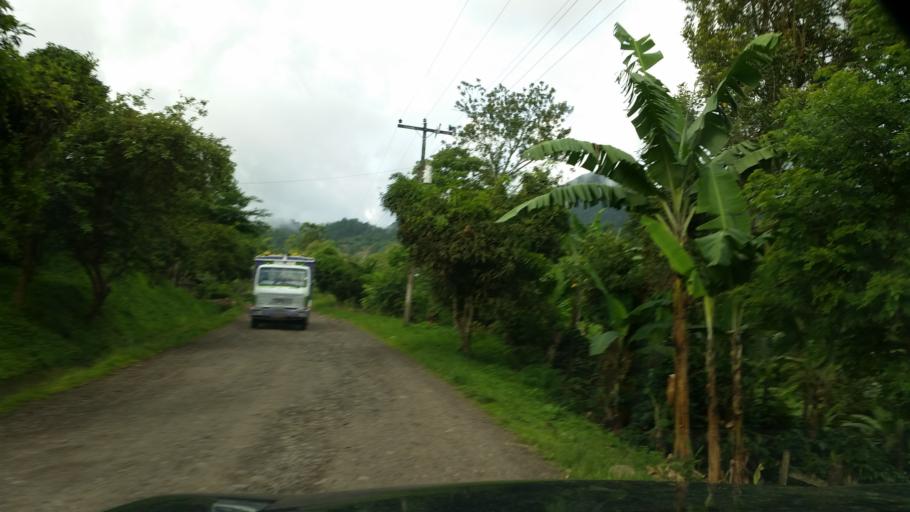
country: NI
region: Jinotega
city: Jinotega
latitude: 13.2611
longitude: -85.7356
